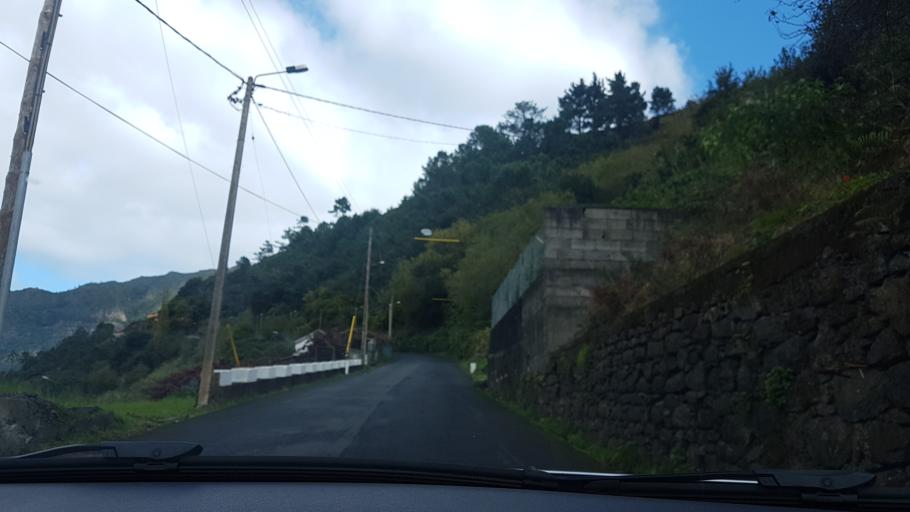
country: PT
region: Madeira
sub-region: Sao Vicente
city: Sao Vicente
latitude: 32.7773
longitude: -17.0312
